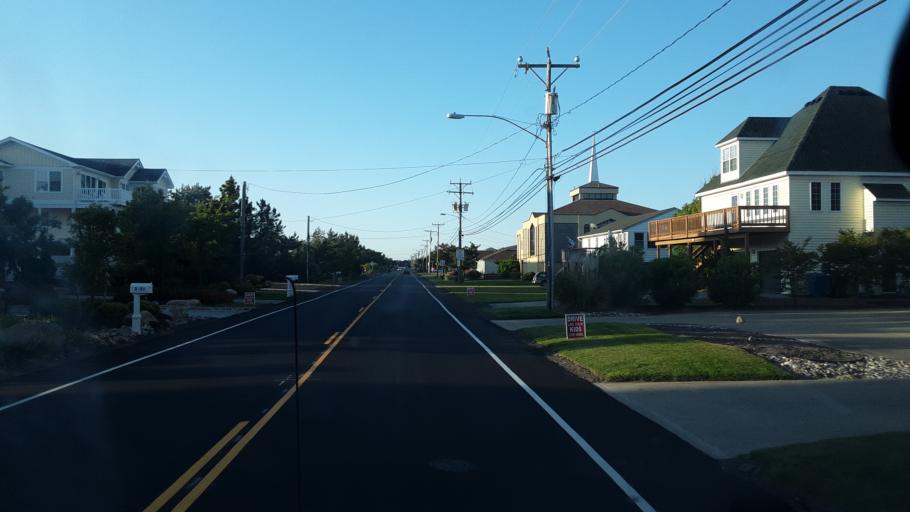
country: US
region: Virginia
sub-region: City of Virginia Beach
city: Virginia Beach
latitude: 36.7241
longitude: -75.9369
